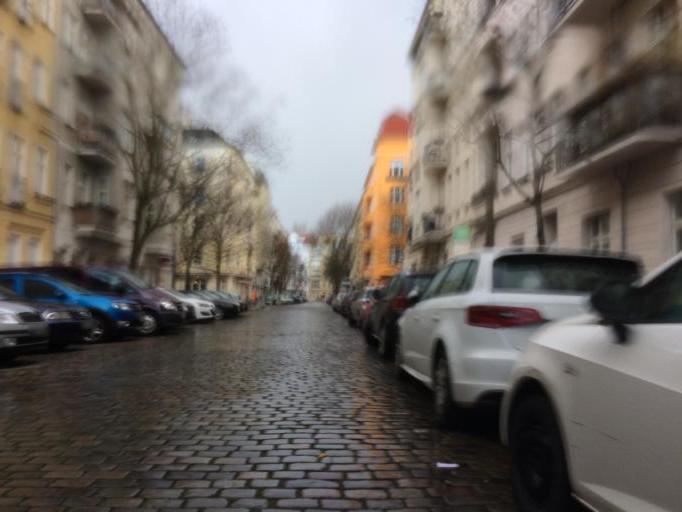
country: DE
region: Berlin
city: Prenzlauer Berg Bezirk
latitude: 52.5325
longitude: 13.4321
